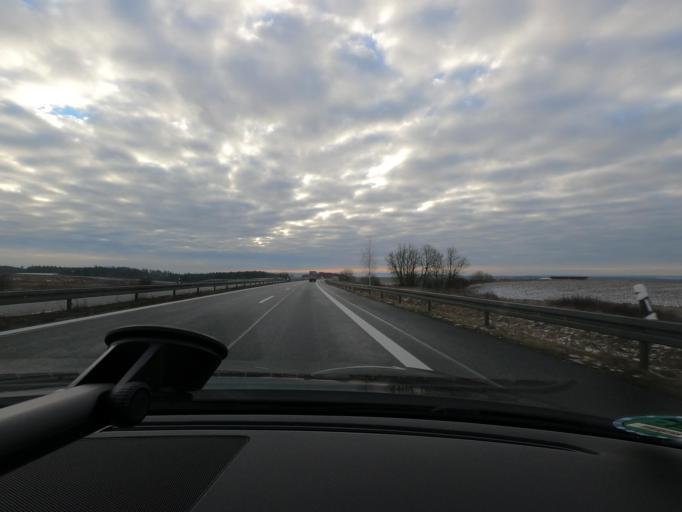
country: DE
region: Bavaria
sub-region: Upper Franconia
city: Meeder
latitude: 50.3352
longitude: 10.9363
